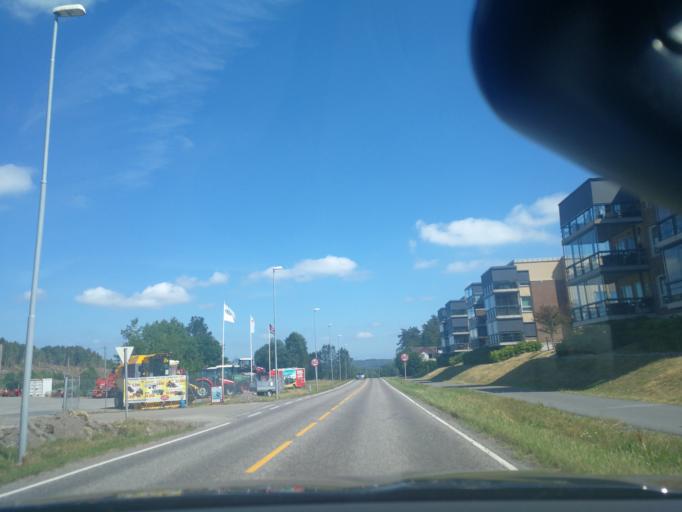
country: NO
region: Vestfold
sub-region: Stokke
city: Stokke
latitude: 59.2234
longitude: 10.3079
